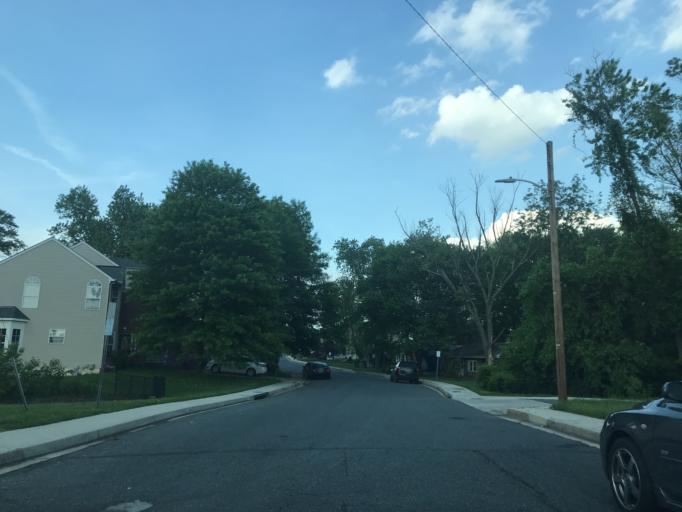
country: US
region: Maryland
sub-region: Harford County
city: Bel Air
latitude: 39.5311
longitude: -76.3527
